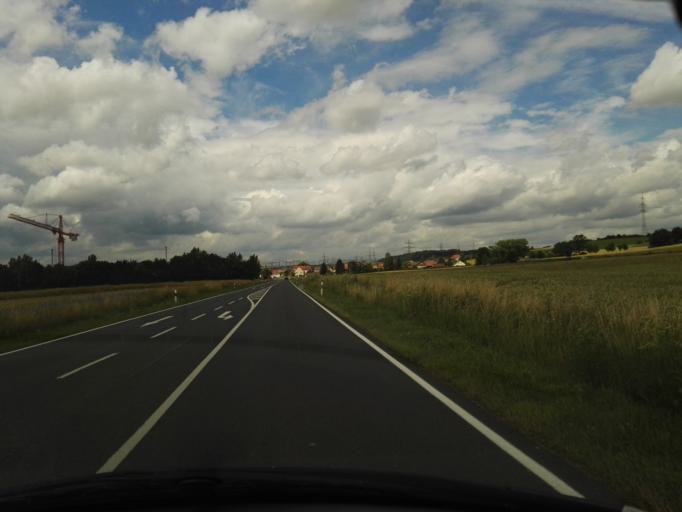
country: DE
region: Bavaria
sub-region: Upper Franconia
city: Redwitz an der Rodach
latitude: 50.1544
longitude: 11.2095
